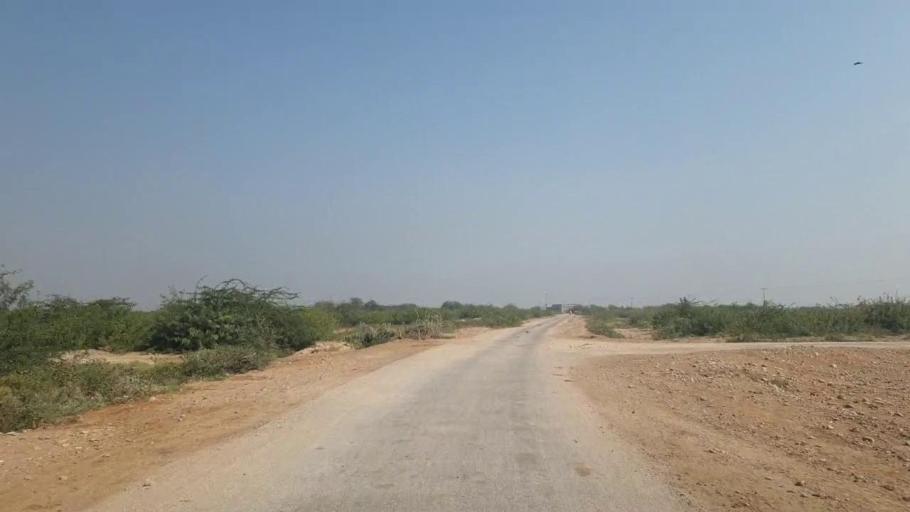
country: PK
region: Sindh
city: Jamshoro
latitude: 25.5395
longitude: 68.3456
